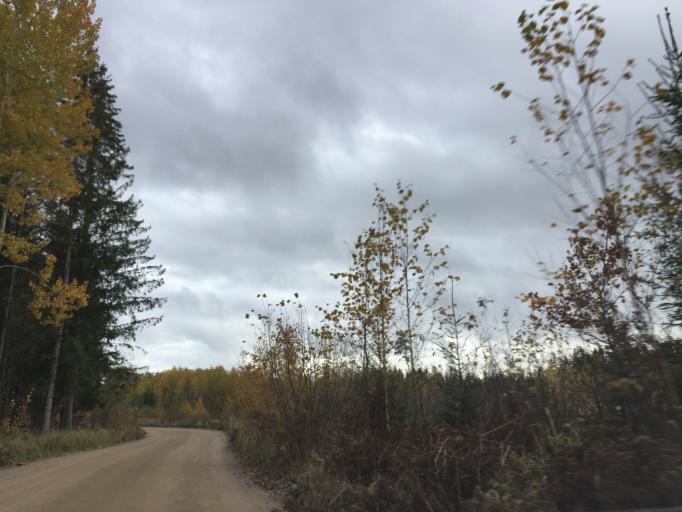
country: LV
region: Salacgrivas
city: Salacgriva
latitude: 57.5703
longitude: 24.3979
